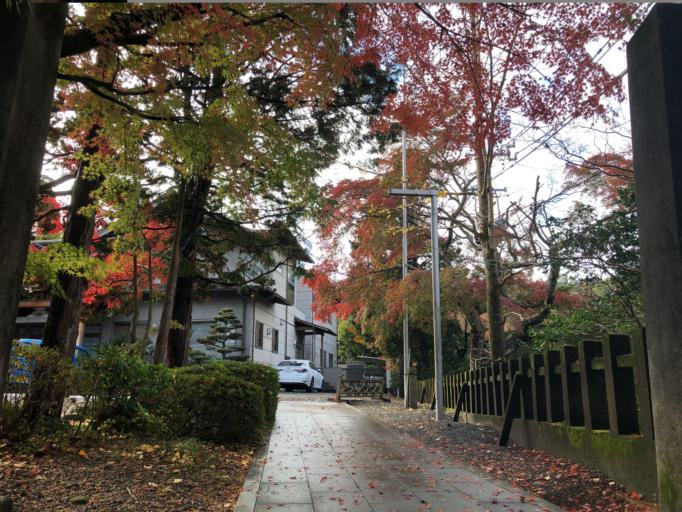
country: JP
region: Shizuoka
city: Kanaya
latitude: 34.8193
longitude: 138.1265
